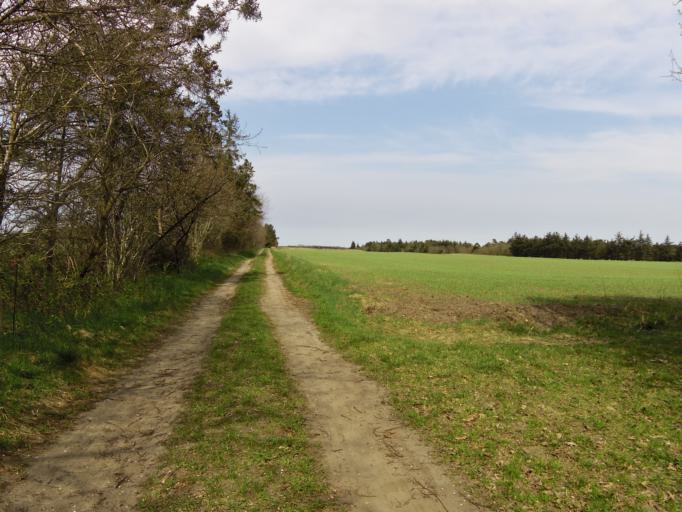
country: DK
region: South Denmark
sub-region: Esbjerg Kommune
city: Ribe
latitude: 55.3167
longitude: 8.8560
